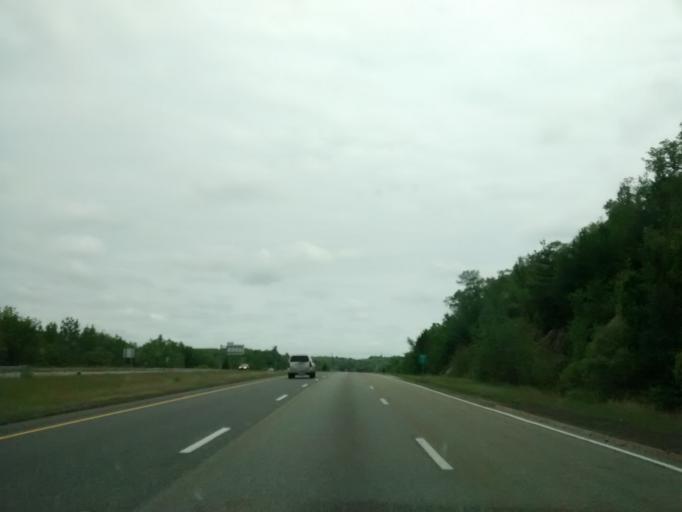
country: US
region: Massachusetts
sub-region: Worcester County
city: Uxbridge
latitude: 42.0417
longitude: -71.6249
